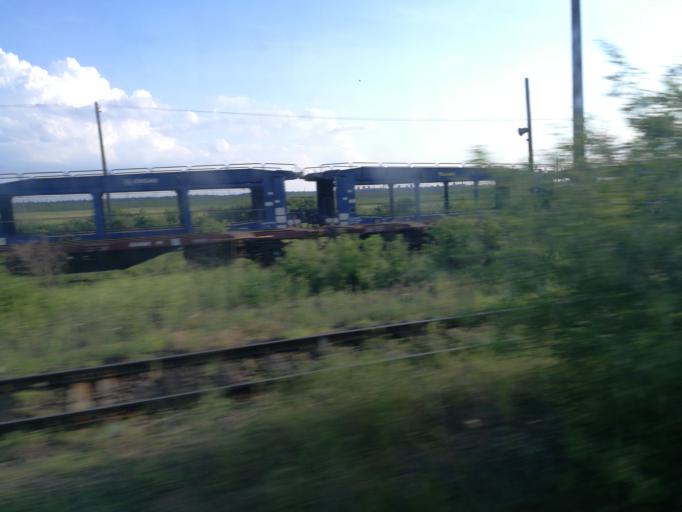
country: RO
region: Arges
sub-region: Oras Stefanesti
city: Golesti
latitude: 44.8323
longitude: 24.9860
